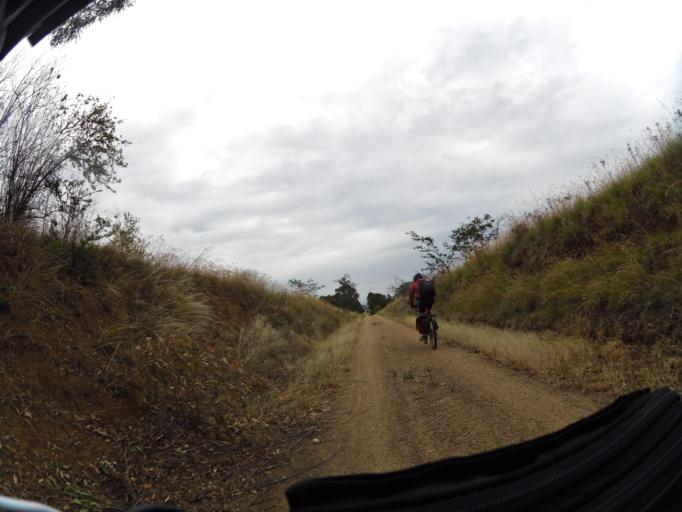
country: AU
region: New South Wales
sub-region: Albury Municipality
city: East Albury
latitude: -36.2114
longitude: 147.0551
